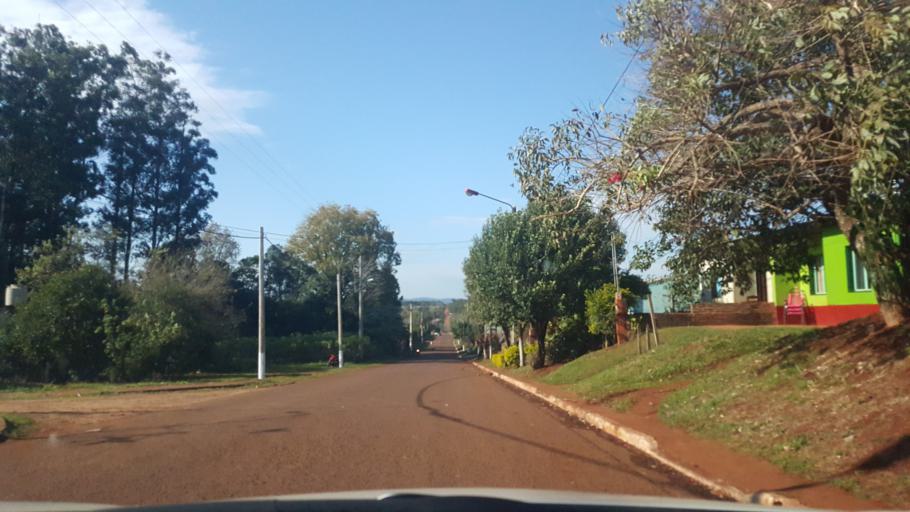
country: AR
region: Misiones
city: Santo Pipo
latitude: -27.1512
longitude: -55.3949
